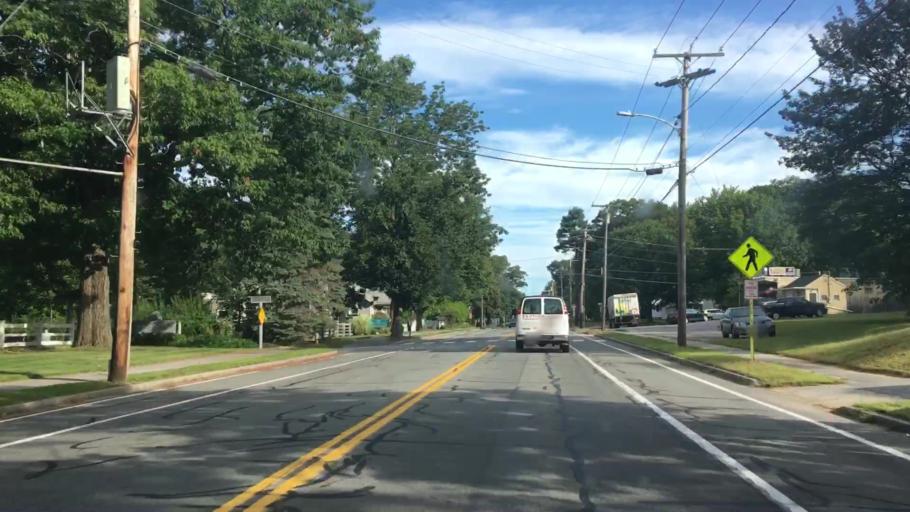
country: US
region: Maine
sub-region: Cumberland County
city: Falmouth
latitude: 43.7125
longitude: -70.2915
